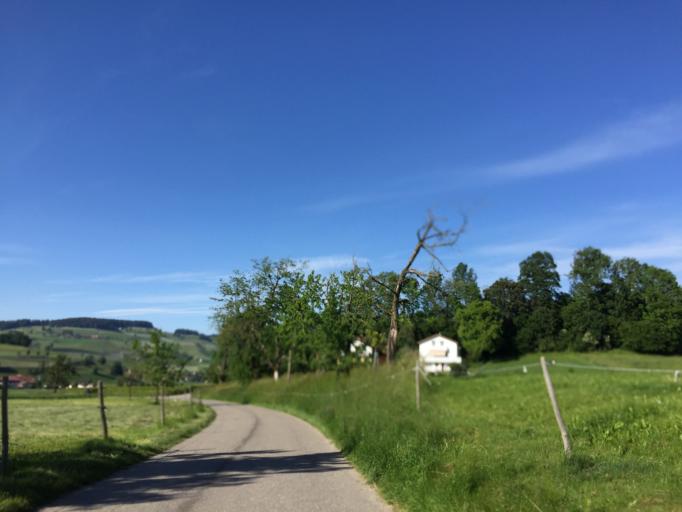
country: CH
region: Bern
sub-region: Bern-Mittelland District
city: Konolfingen
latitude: 46.8792
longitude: 7.6368
